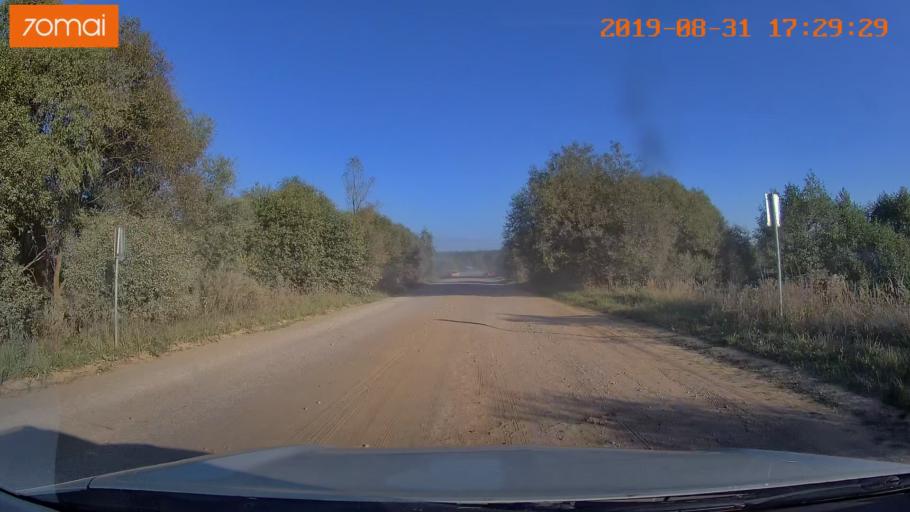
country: RU
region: Kaluga
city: Detchino
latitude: 54.8130
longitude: 36.3260
